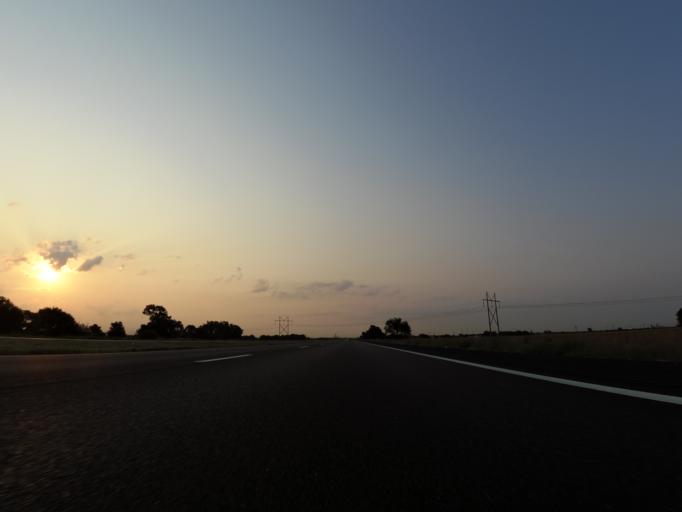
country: US
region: Kansas
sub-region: Sedgwick County
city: Maize
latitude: 37.7983
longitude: -97.4865
